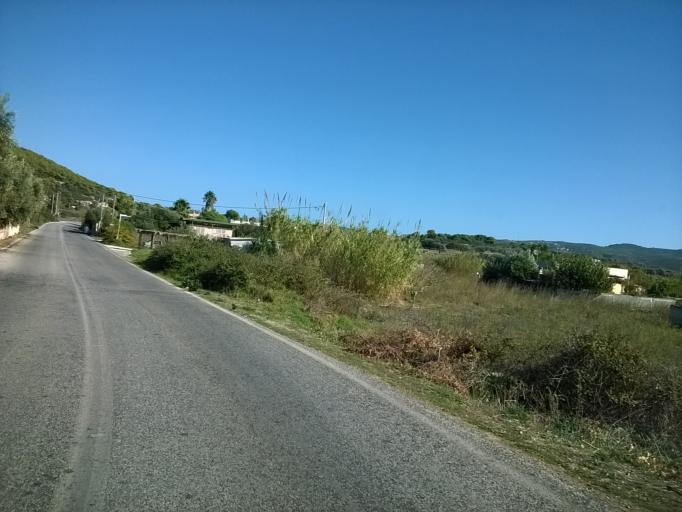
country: GR
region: Attica
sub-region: Nomarchia Anatolikis Attikis
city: Anavyssos
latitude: 37.7520
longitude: 23.9566
